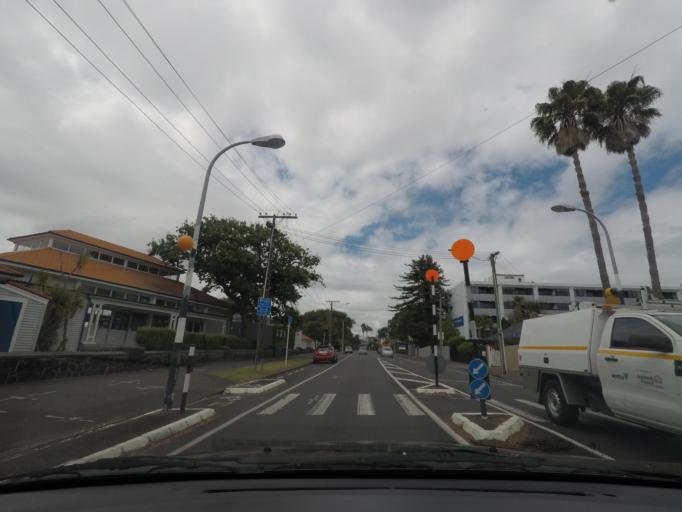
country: NZ
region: Auckland
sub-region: Auckland
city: Auckland
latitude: -36.8550
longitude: 174.7870
